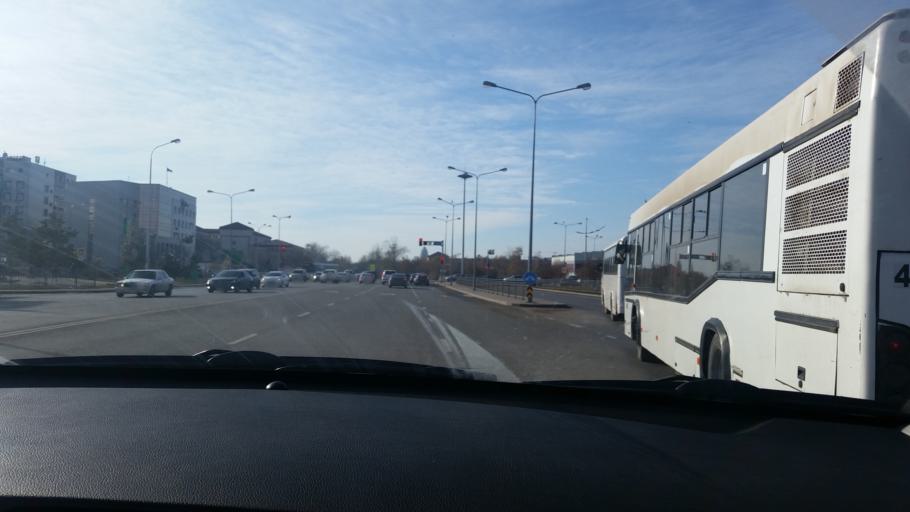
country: KZ
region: Astana Qalasy
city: Astana
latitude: 51.1518
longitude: 71.4582
